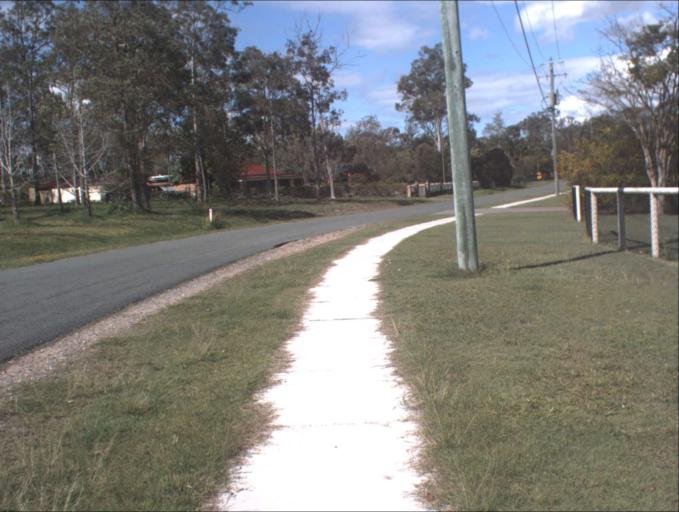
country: AU
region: Queensland
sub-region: Logan
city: Park Ridge South
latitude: -27.7436
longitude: 153.0372
